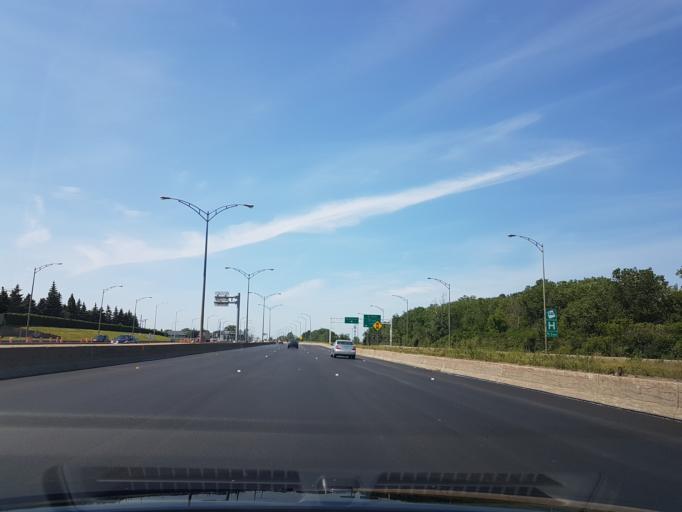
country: CA
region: Quebec
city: Cote-Saint-Luc
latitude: 45.4477
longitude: -73.6882
